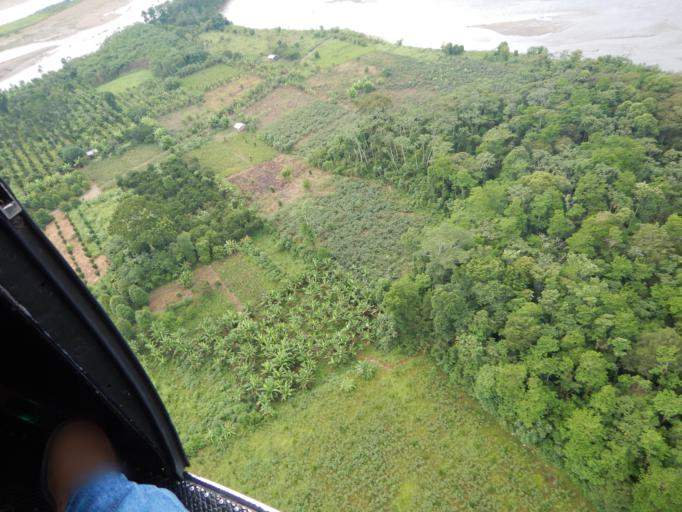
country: BO
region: Cochabamba
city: Chimore
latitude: -16.9671
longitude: -65.0978
